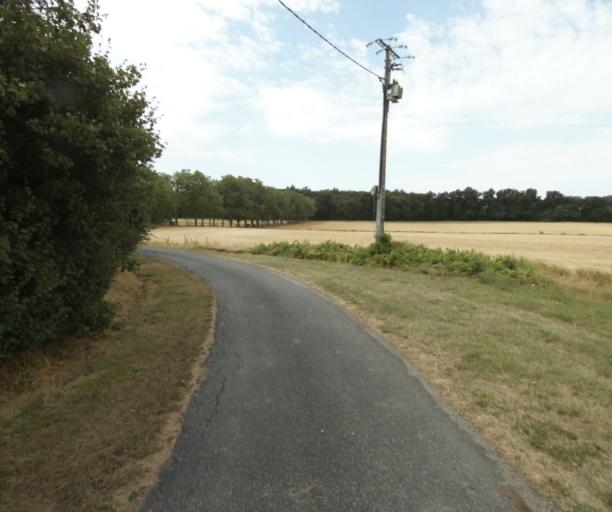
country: FR
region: Midi-Pyrenees
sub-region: Departement de la Haute-Garonne
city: Saint-Felix-Lauragais
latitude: 43.4322
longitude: 1.9256
